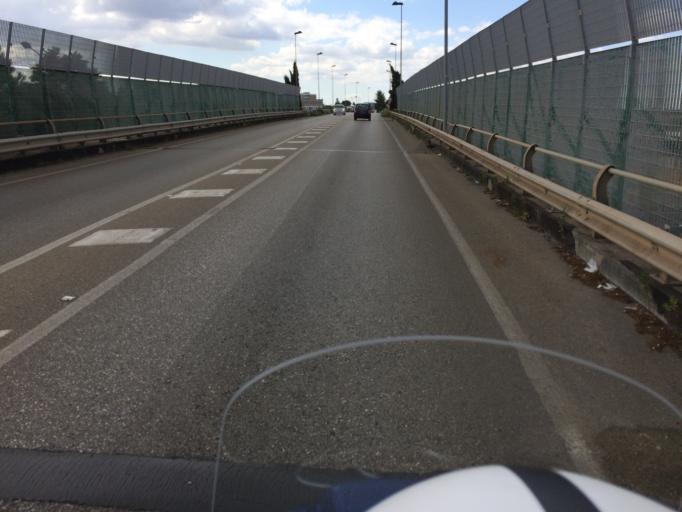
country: IT
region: Apulia
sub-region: Provincia di Bari
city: Bari
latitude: 41.0968
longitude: 16.8296
